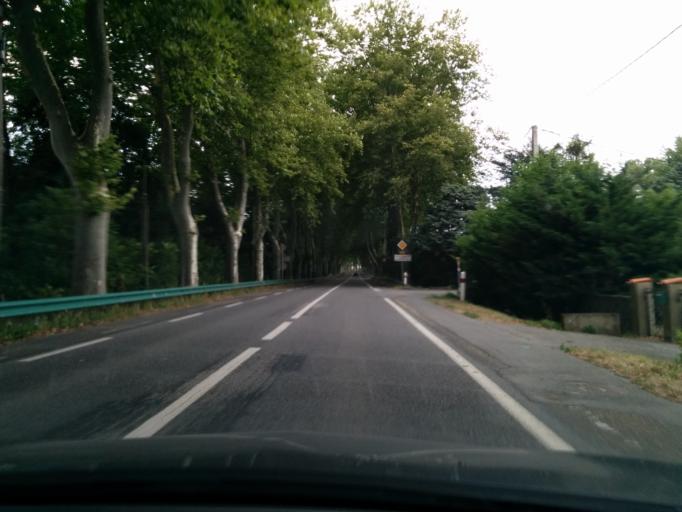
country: FR
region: Midi-Pyrenees
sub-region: Departement de la Haute-Garonne
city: Villefranche-de-Lauragais
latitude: 43.4087
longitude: 1.7066
